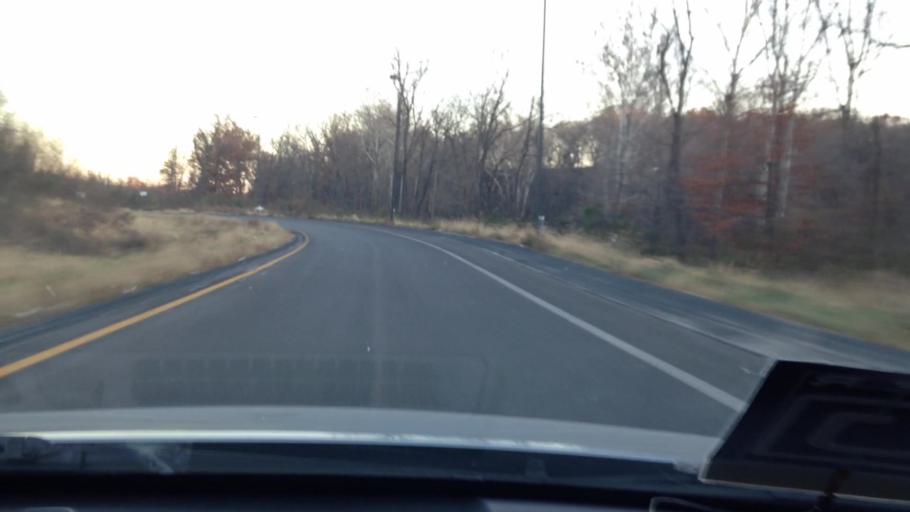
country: US
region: Missouri
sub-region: Clay County
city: Gladstone
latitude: 39.2577
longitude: -94.5600
